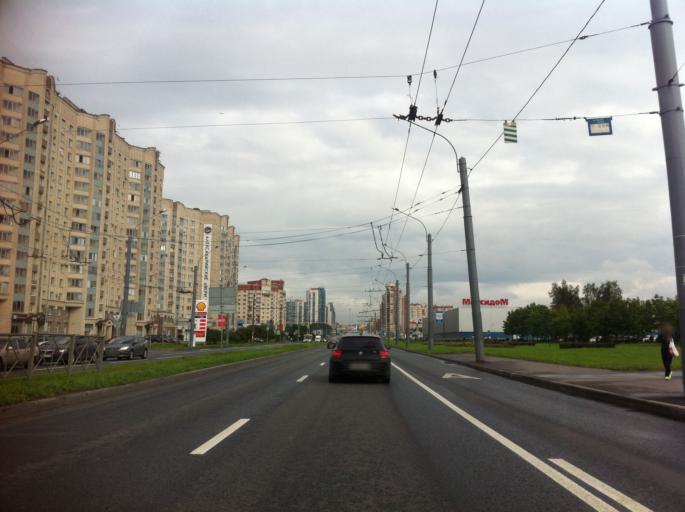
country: RU
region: St.-Petersburg
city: Dachnoye
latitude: 59.8519
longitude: 30.2229
